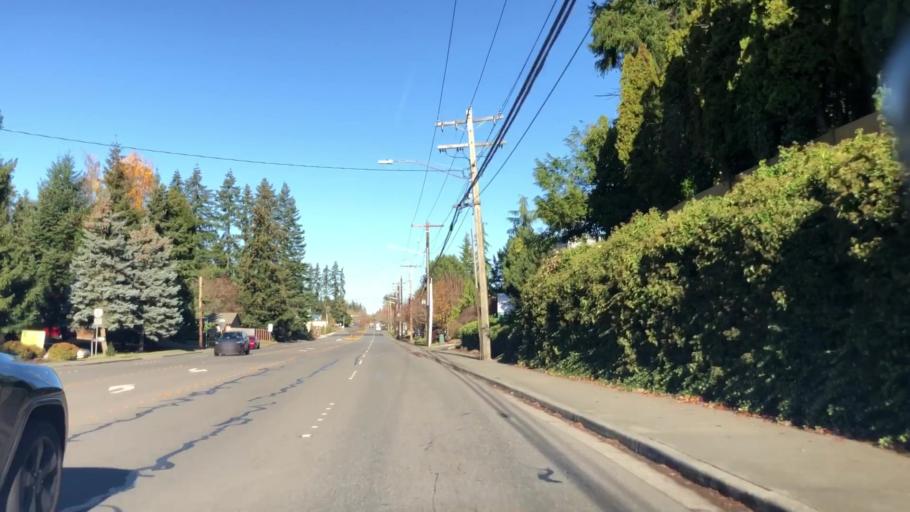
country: US
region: Washington
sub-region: Snohomish County
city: Alderwood Manor
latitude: 47.8234
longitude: -122.2817
